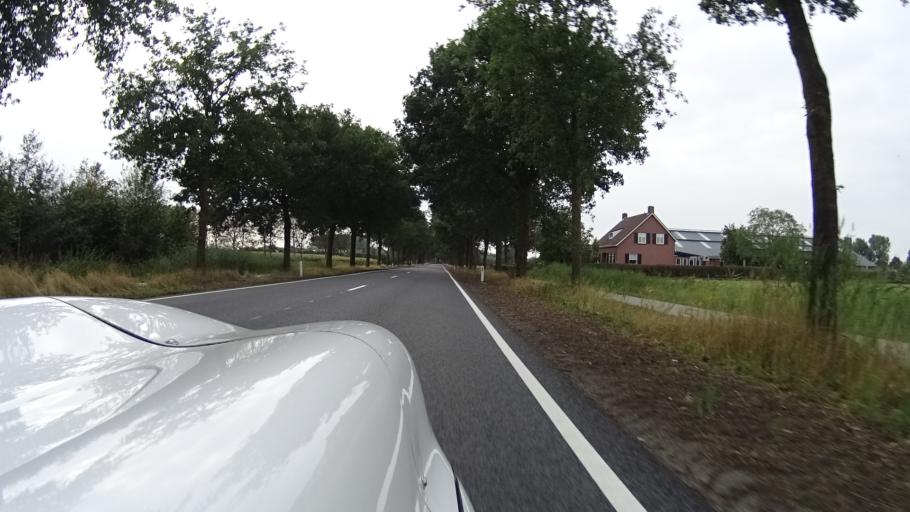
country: NL
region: North Brabant
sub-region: Gemeente Boekel
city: Boekel
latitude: 51.5703
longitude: 5.6635
